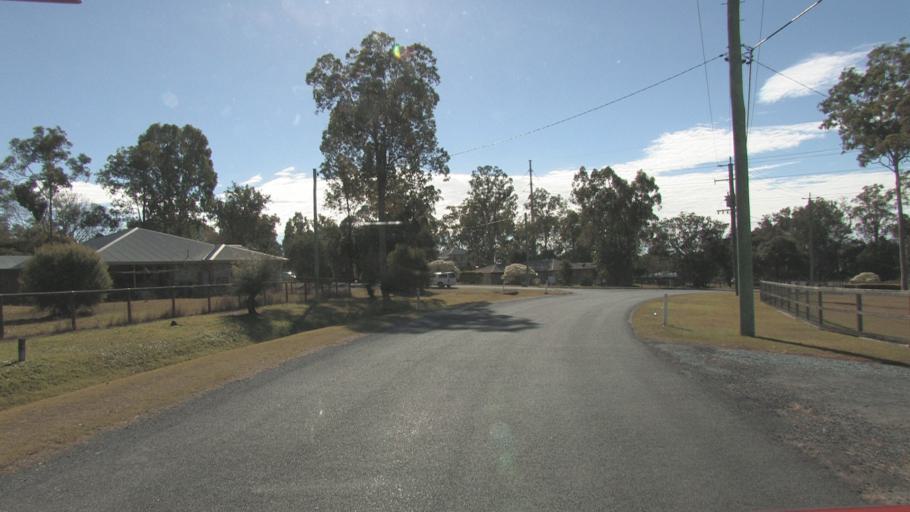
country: AU
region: Queensland
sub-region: Logan
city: Chambers Flat
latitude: -27.7744
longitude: 153.0786
